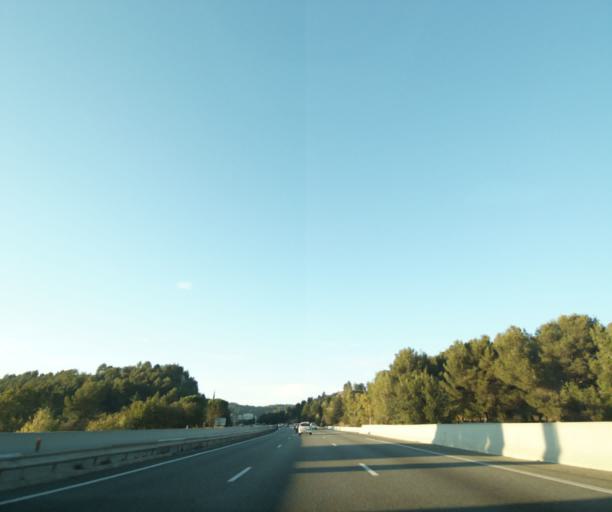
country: FR
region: Provence-Alpes-Cote d'Azur
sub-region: Departement des Bouches-du-Rhone
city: Le Tholonet
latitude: 43.4962
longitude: 5.5252
